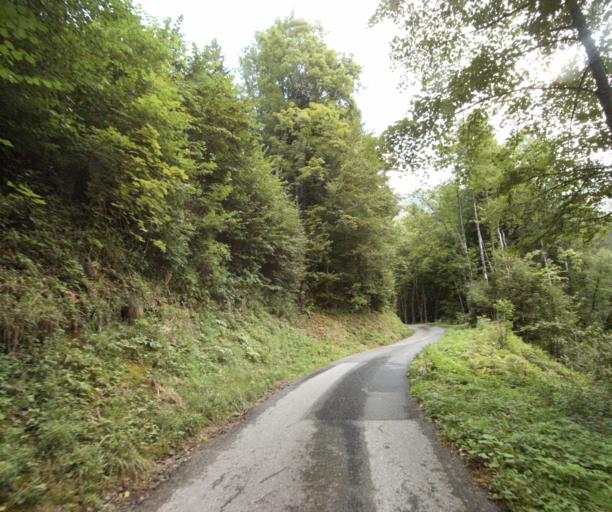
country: CH
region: Vaud
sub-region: Riviera-Pays-d'Enhaut District
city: Caux
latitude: 46.4174
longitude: 6.9693
